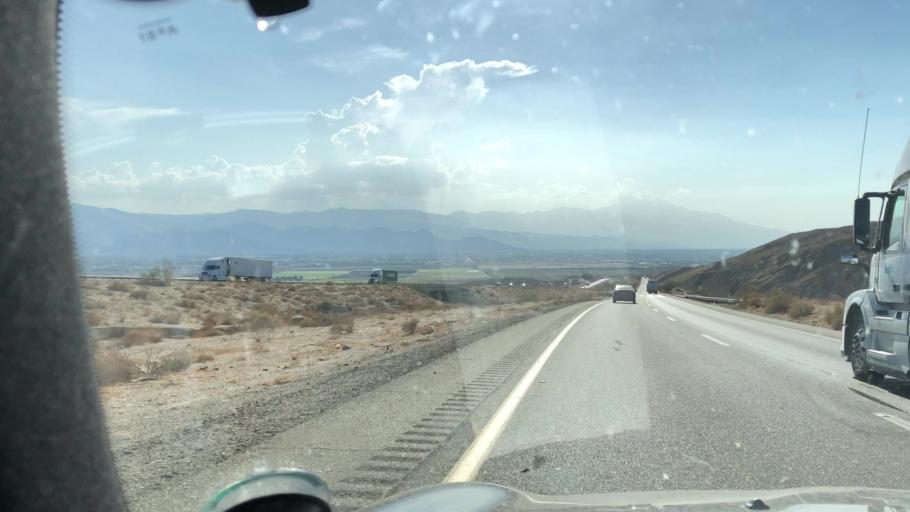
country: US
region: California
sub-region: Riverside County
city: Thermal
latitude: 33.6986
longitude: -116.1034
